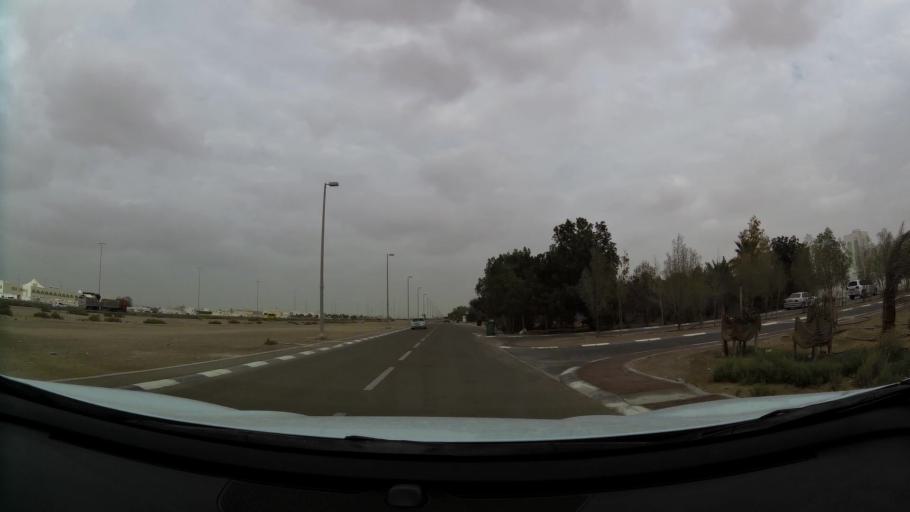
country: AE
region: Abu Dhabi
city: Abu Dhabi
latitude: 24.3467
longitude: 54.6508
